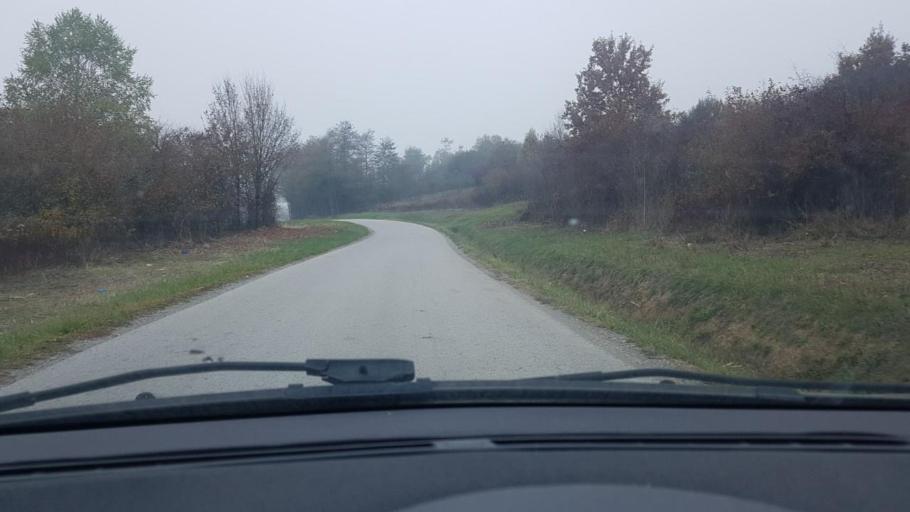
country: HR
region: Krapinsko-Zagorska
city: Marija Bistrica
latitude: 46.0675
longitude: 16.1789
